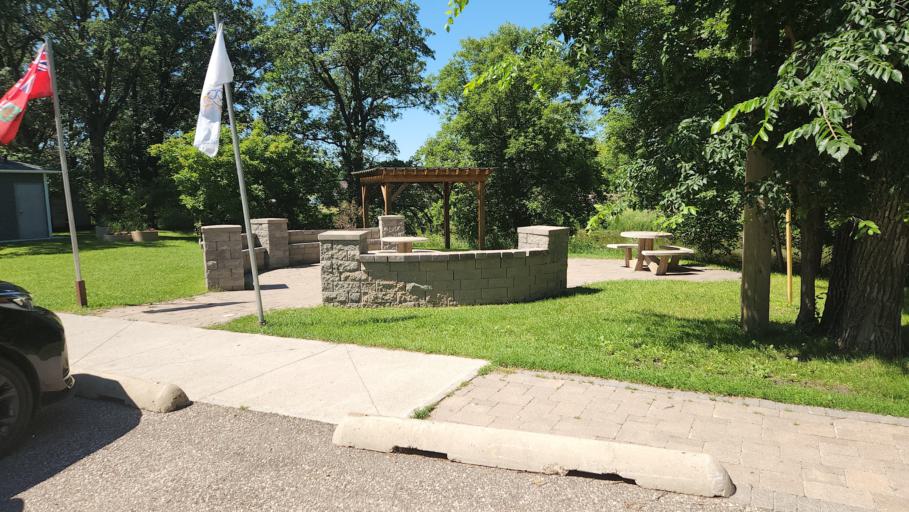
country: CA
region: Manitoba
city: Souris
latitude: 49.6164
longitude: -100.2542
